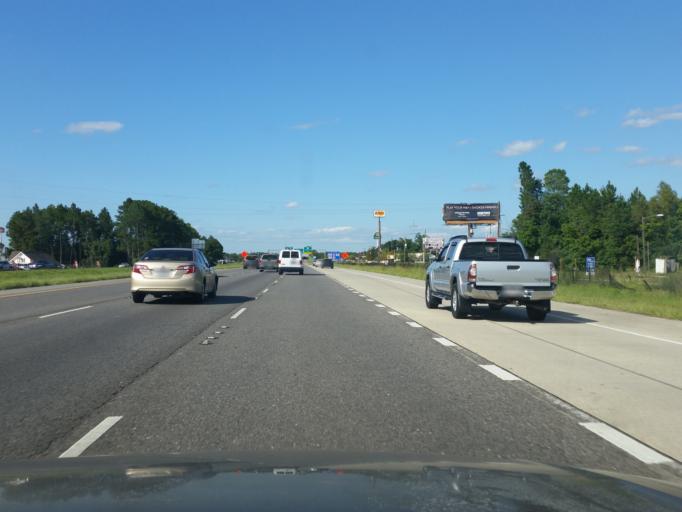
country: US
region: Louisiana
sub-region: Saint Tammany Parish
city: Slidell
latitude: 30.2774
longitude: -89.7522
